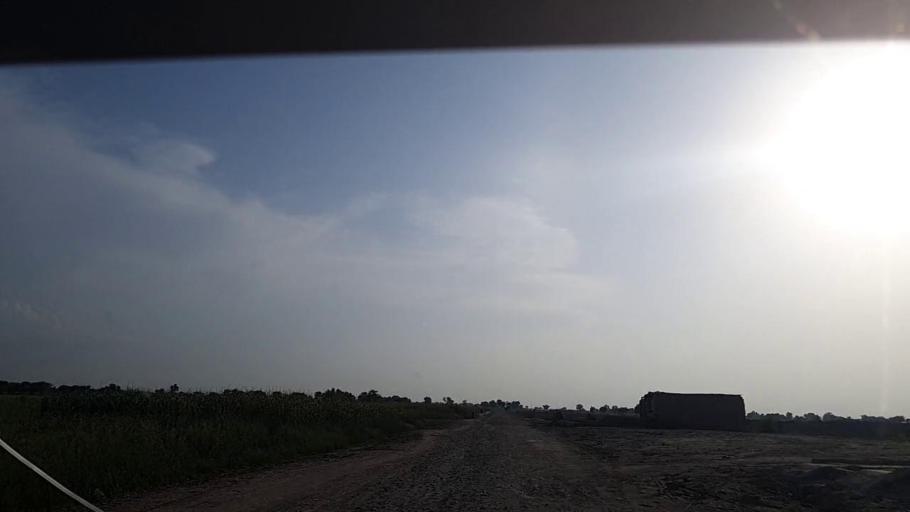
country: PK
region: Sindh
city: Khanpur
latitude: 27.8292
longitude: 69.3558
